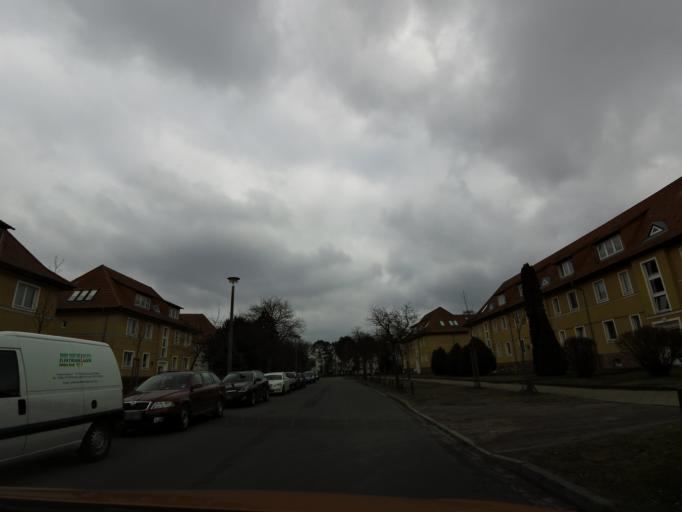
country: DE
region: Brandenburg
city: Rathenow
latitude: 52.6087
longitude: 12.3502
